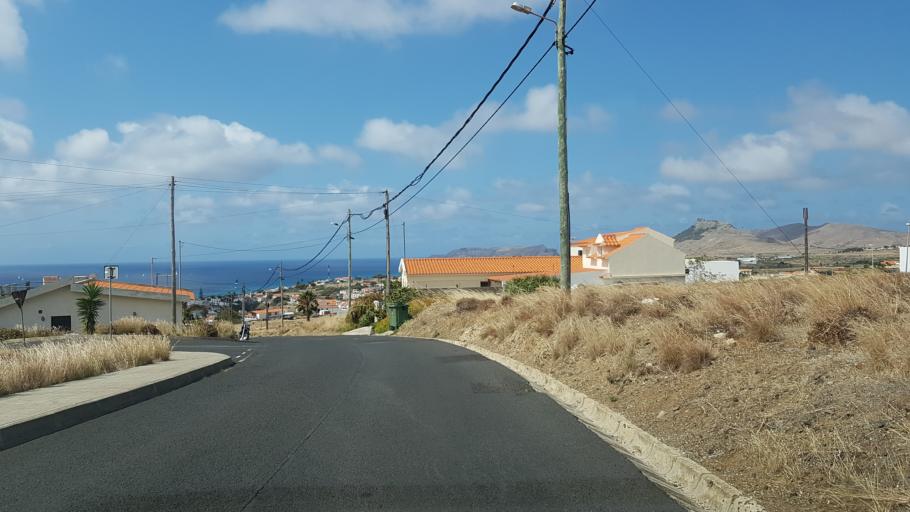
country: PT
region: Madeira
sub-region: Porto Santo
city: Vila de Porto Santo
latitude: 33.0700
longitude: -16.3324
